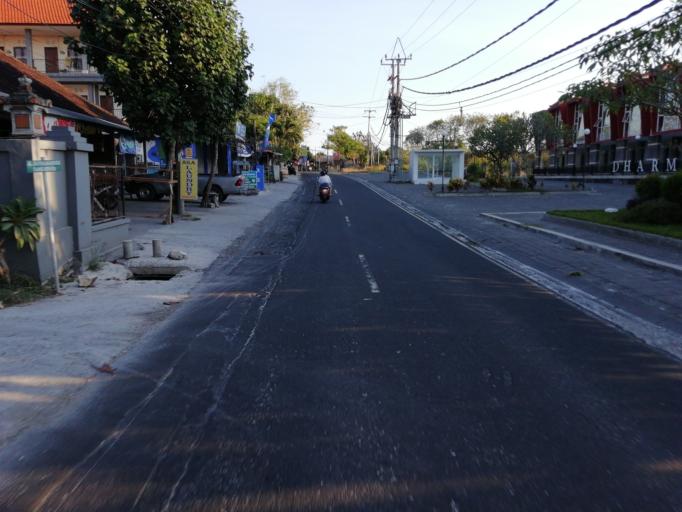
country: ID
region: Bali
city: Bualu
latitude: -8.8183
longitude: 115.1902
